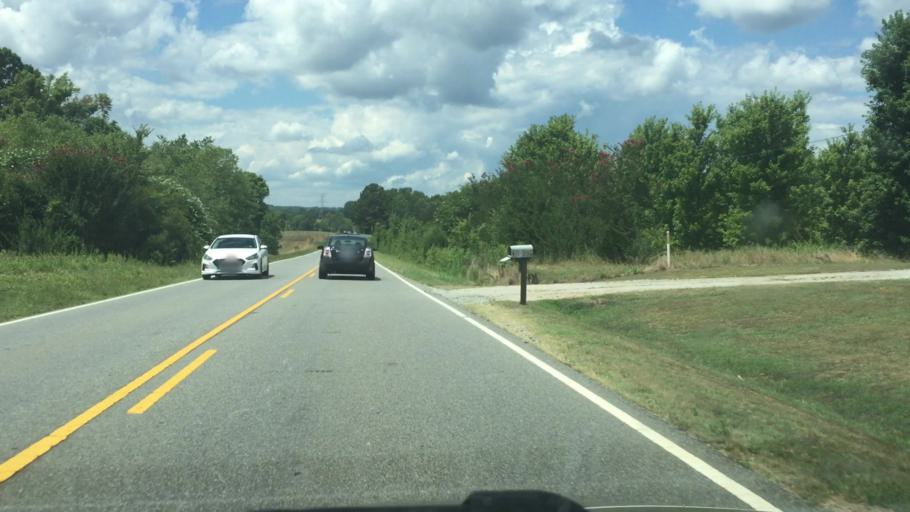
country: US
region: North Carolina
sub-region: Rowan County
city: Enochville
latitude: 35.4867
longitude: -80.6926
